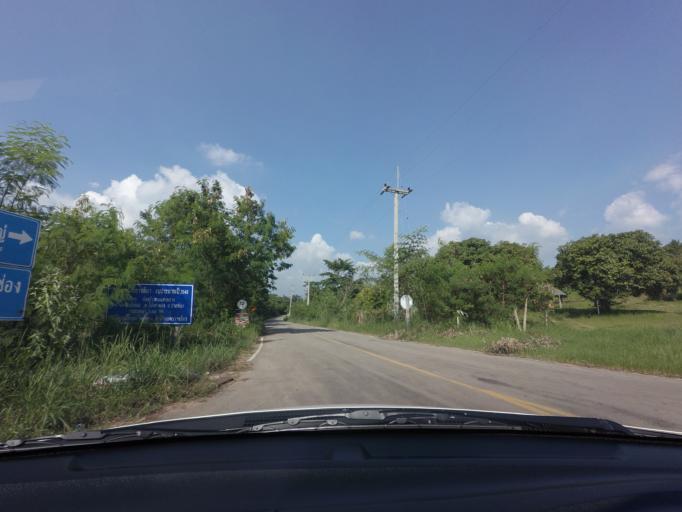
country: TH
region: Nakhon Ratchasima
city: Wang Nam Khiao
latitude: 14.4809
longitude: 101.6243
